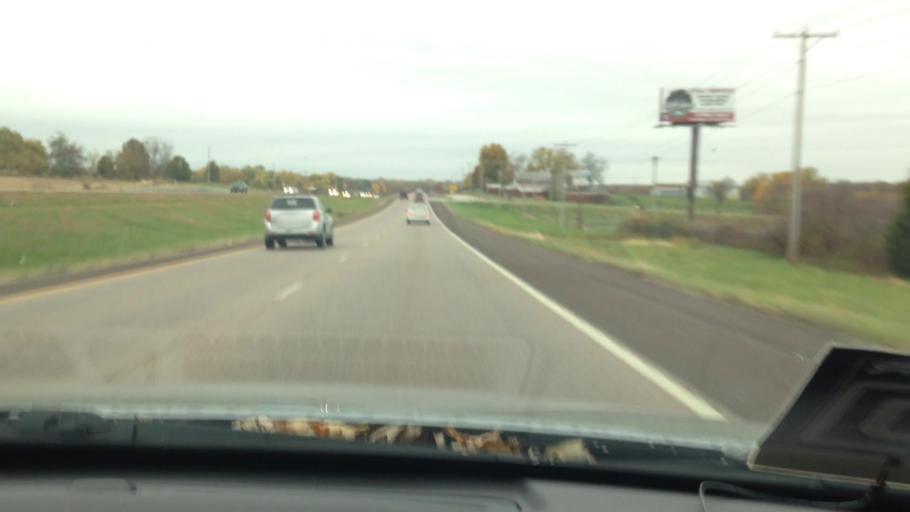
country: US
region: Kansas
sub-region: Leavenworth County
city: Basehor
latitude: 39.1535
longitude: -94.8951
